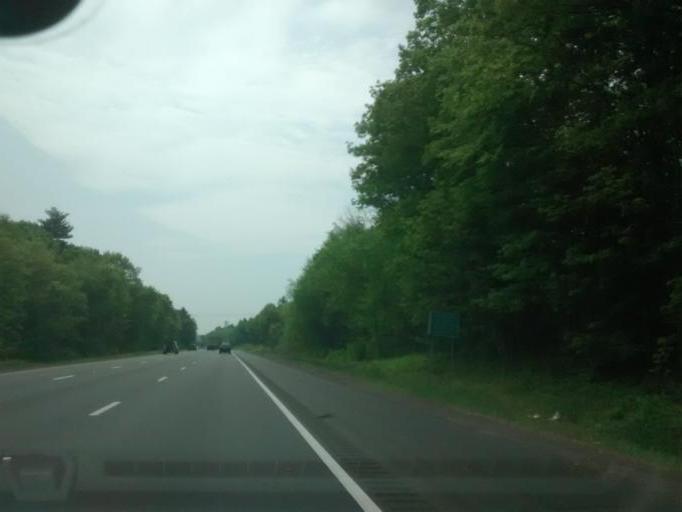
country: US
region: Massachusetts
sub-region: Worcester County
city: Milford
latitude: 42.1342
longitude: -71.4787
